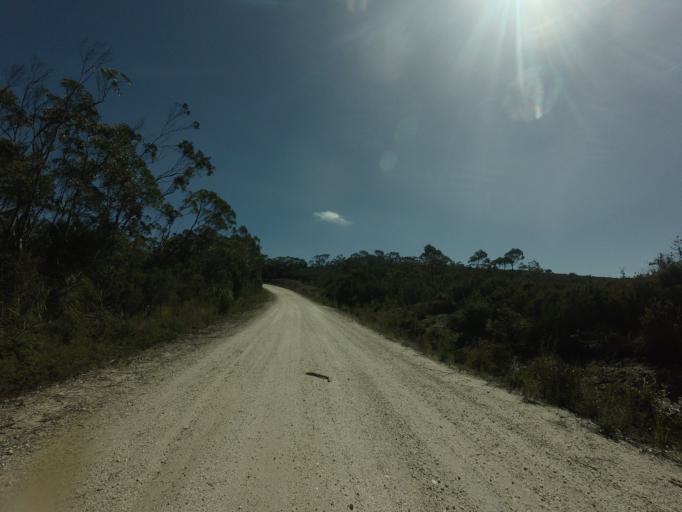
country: AU
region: Tasmania
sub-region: Huon Valley
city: Geeveston
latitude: -43.0406
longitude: 146.2749
